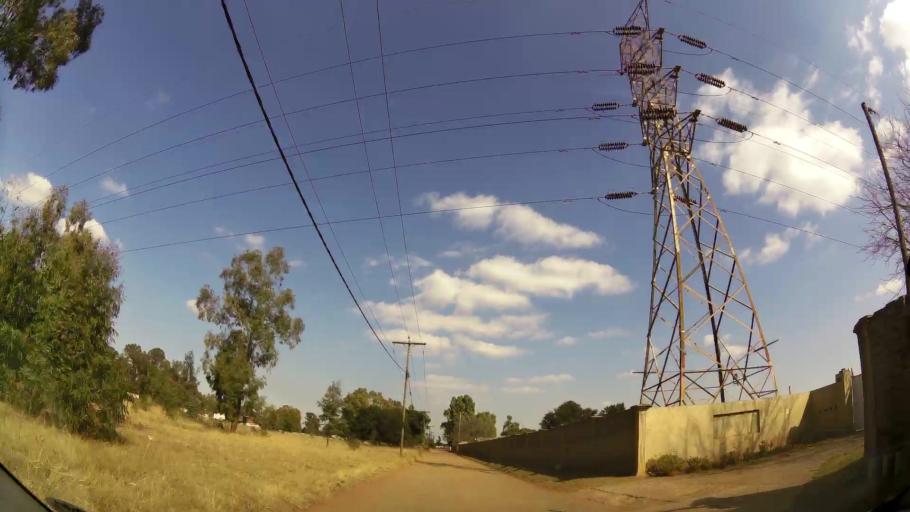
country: ZA
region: Gauteng
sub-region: Ekurhuleni Metropolitan Municipality
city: Benoni
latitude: -26.1084
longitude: 28.3617
